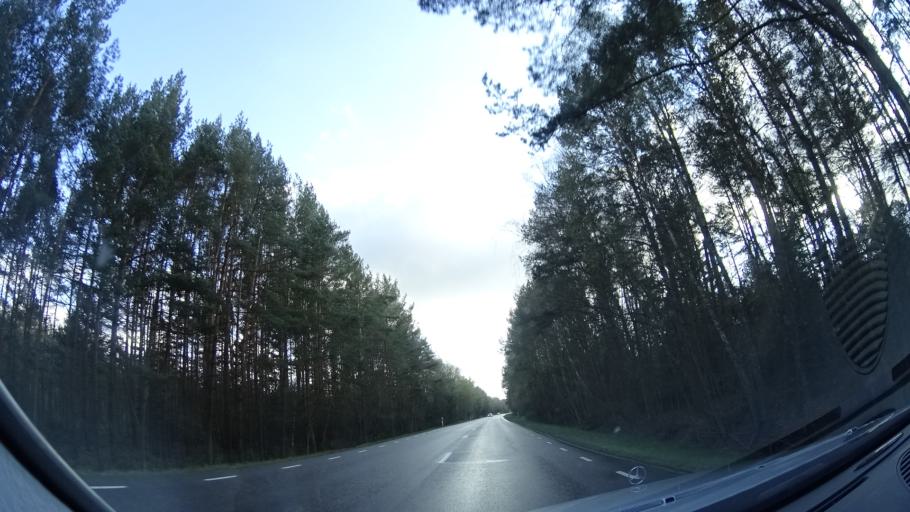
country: SE
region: Skane
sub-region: Klippans Kommun
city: Ljungbyhed
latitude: 56.0878
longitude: 13.2777
